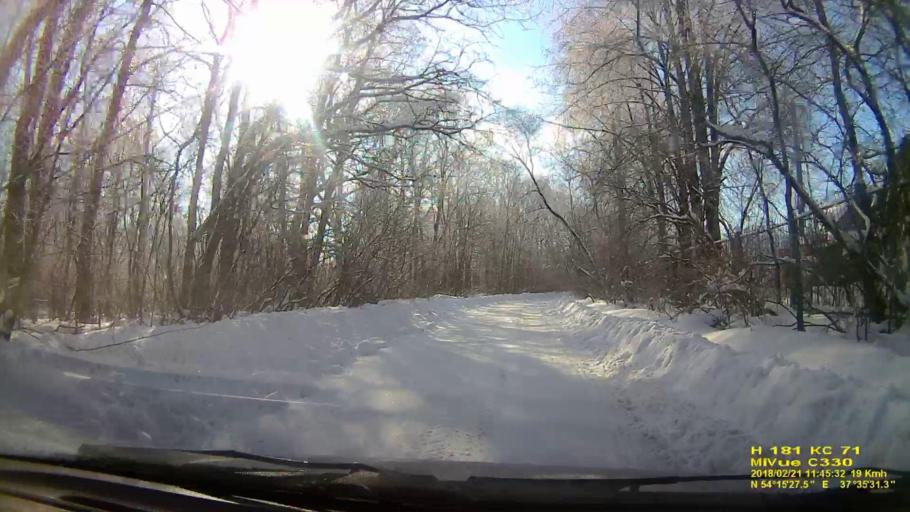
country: RU
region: Tula
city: Gorelki
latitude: 54.2576
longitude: 37.5920
